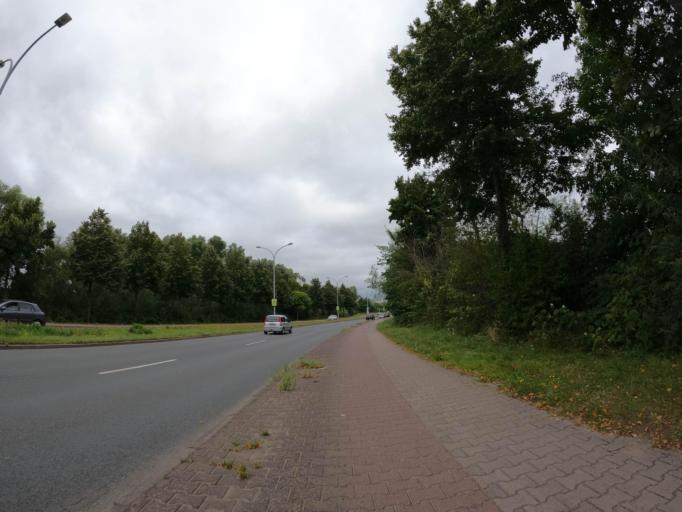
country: DE
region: Mecklenburg-Vorpommern
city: Stralsund
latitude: 54.3159
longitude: 13.0442
